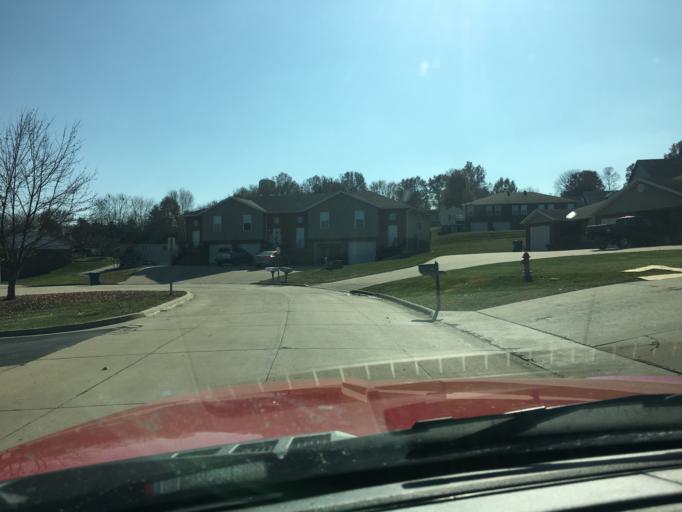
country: US
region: Missouri
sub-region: Cole County
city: Wardsville
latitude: 38.4879
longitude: -92.1741
